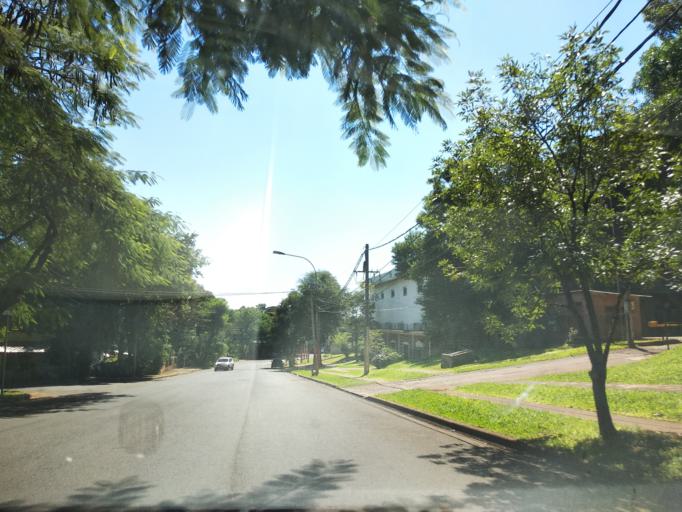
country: AR
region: Misiones
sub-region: Departamento de Iguazu
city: Puerto Iguazu
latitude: -25.6025
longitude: -54.5666
